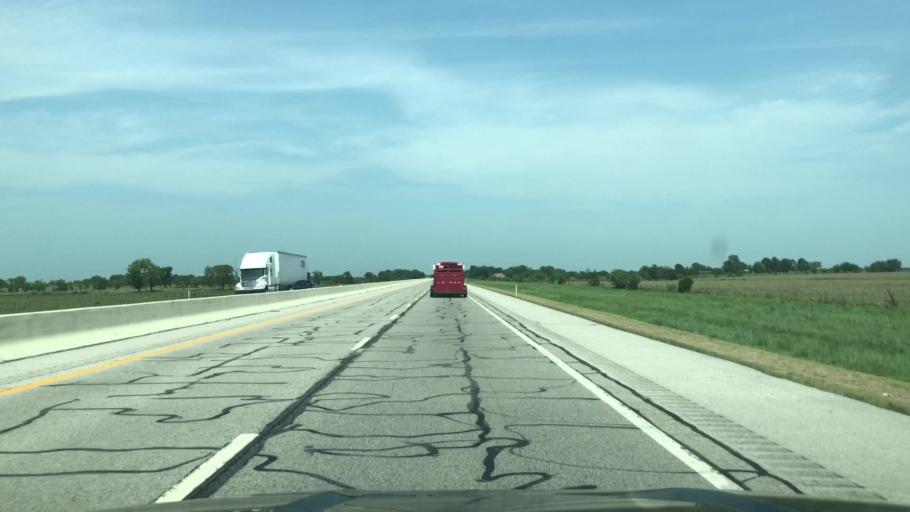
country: US
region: Oklahoma
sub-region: Craig County
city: Vinita
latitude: 36.5152
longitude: -95.2653
